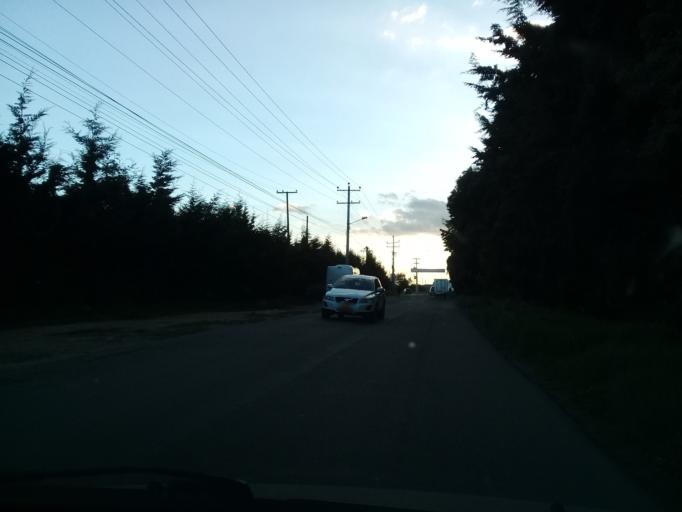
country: CO
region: Cundinamarca
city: Cota
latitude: 4.7787
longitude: -74.1600
